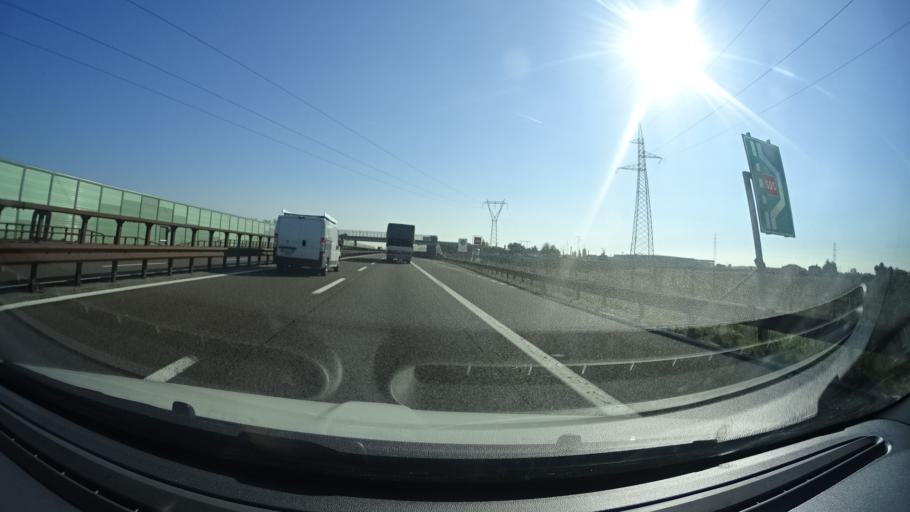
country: IT
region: Veneto
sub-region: Provincia di Verona
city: Bussolengo
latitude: 45.4543
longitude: 10.8587
